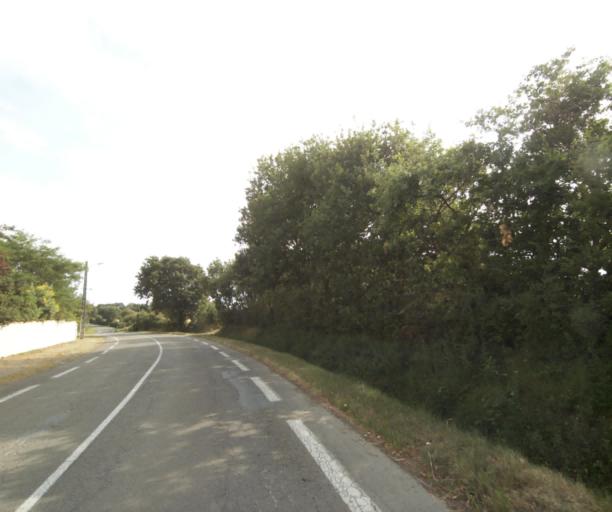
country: FR
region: Pays de la Loire
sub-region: Departement de la Vendee
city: Chateau-d'Olonne
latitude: 46.5004
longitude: -1.7336
